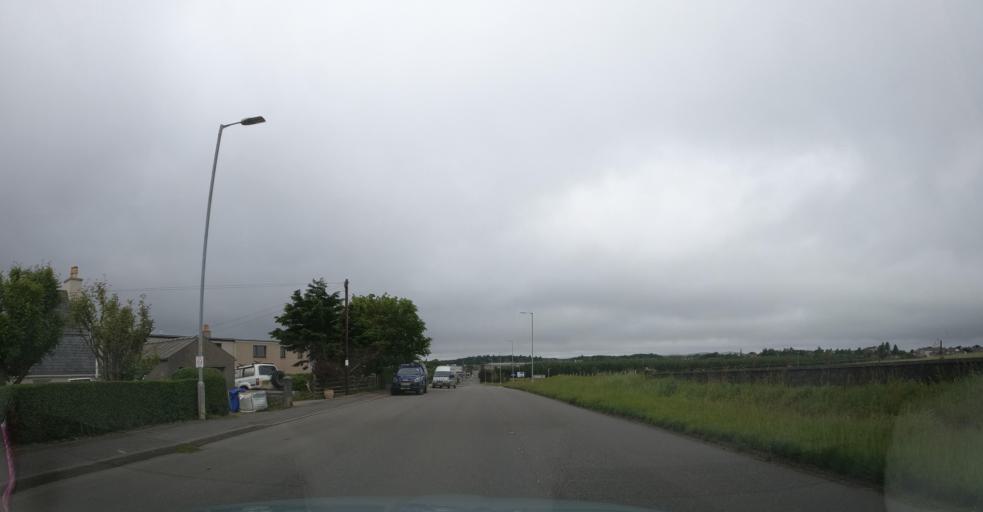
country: GB
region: Scotland
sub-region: Eilean Siar
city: Stornoway
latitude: 58.2083
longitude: -6.3670
